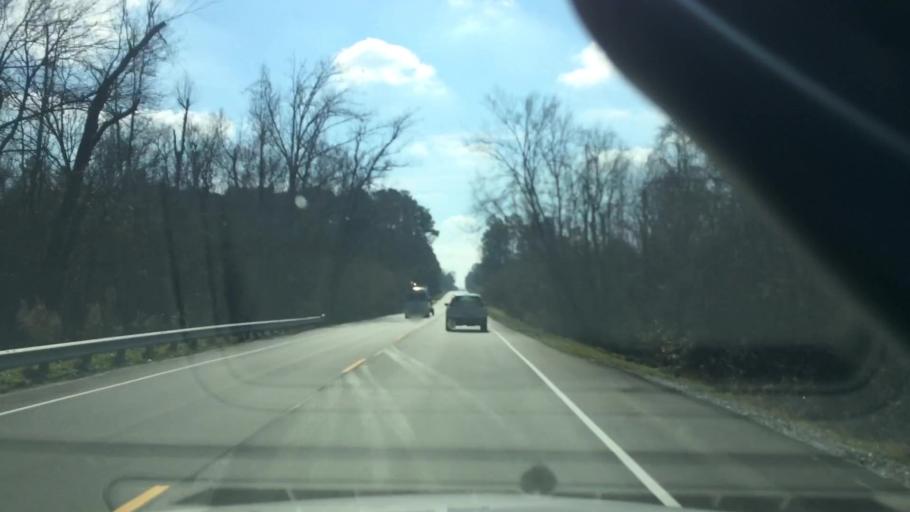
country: US
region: North Carolina
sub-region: Duplin County
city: Beulaville
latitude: 34.9416
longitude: -77.7693
